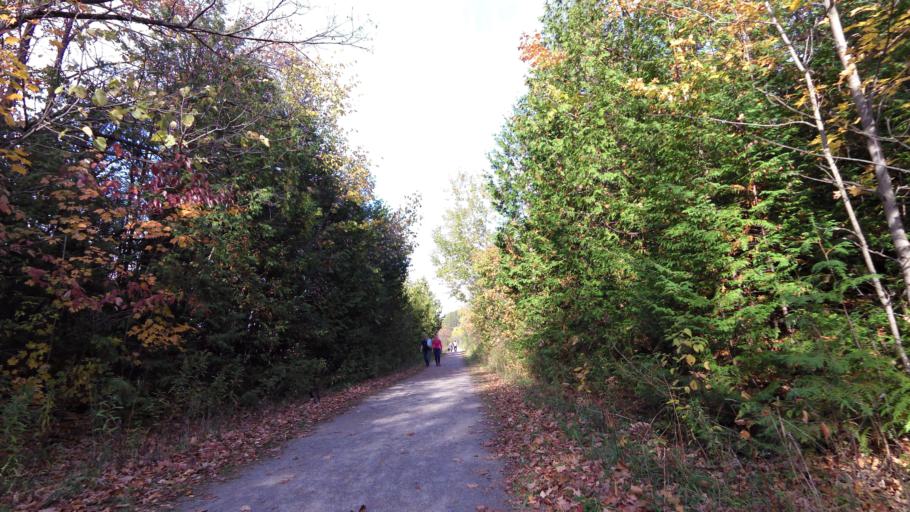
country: CA
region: Ontario
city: Orangeville
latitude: 43.8147
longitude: -80.0276
